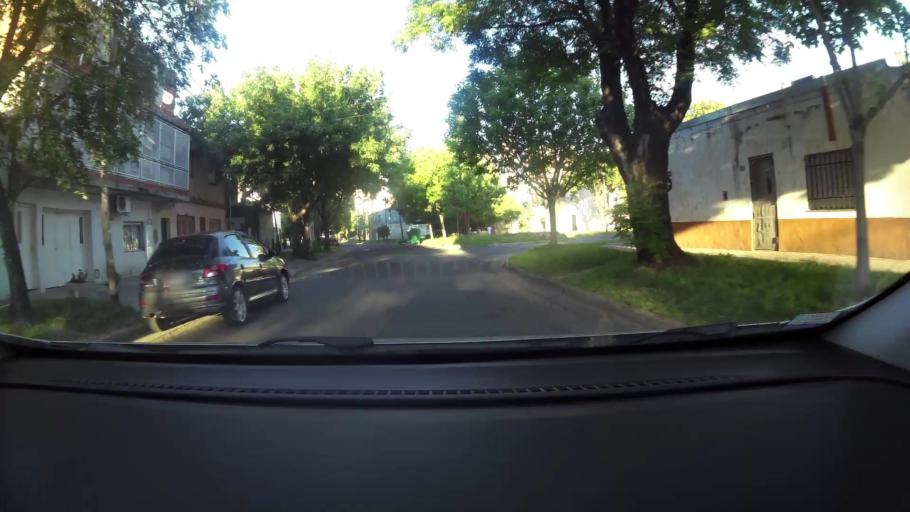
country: AR
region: Santa Fe
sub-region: Departamento de Rosario
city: Rosario
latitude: -32.9676
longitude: -60.6688
